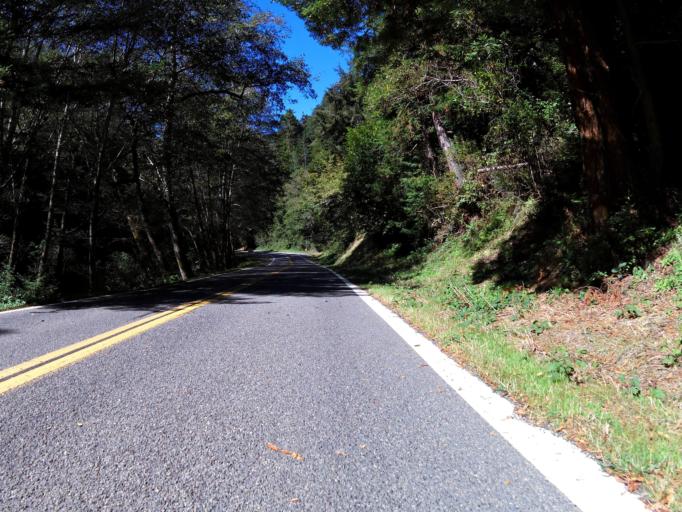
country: US
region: California
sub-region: Mendocino County
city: Fort Bragg
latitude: 39.7803
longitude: -123.8271
